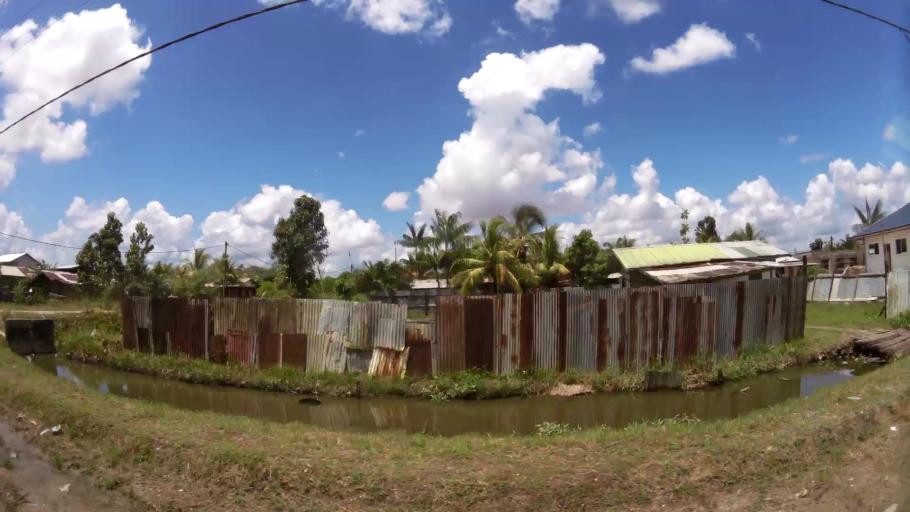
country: SR
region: Paramaribo
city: Paramaribo
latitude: 5.8536
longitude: -55.1689
